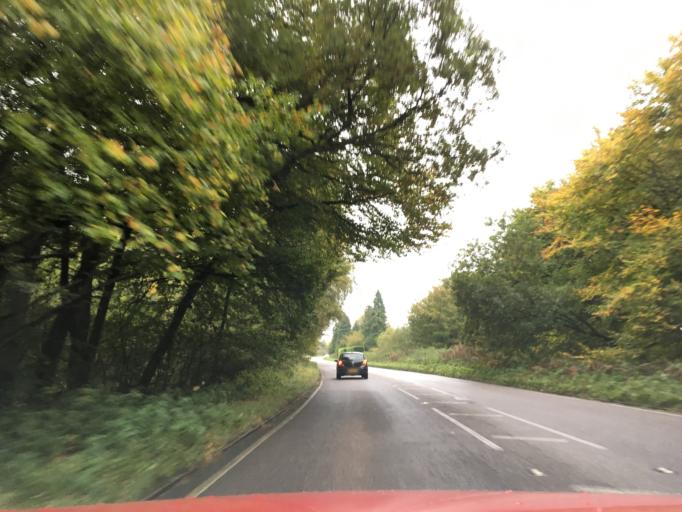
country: GB
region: England
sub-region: West Berkshire
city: Welford
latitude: 51.4273
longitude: -1.4029
